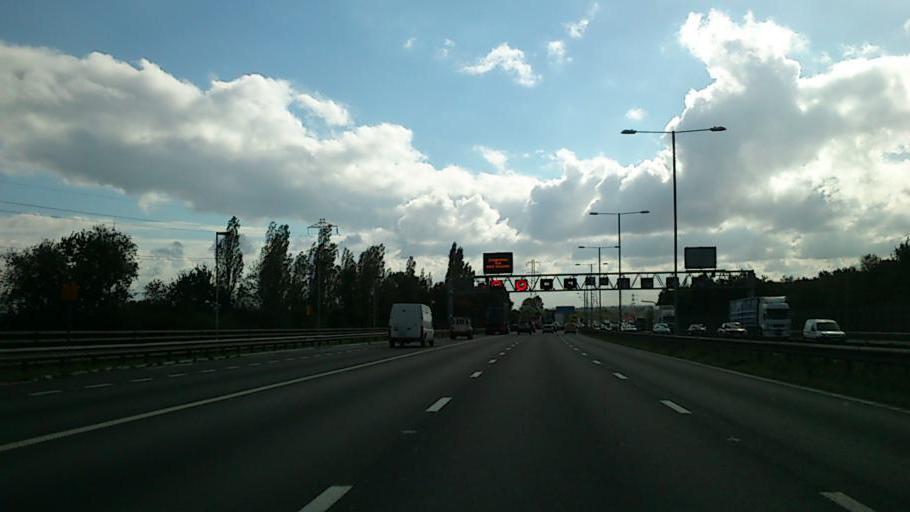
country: GB
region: England
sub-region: Walsall
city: Bloxwich
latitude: 52.6097
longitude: -2.0229
